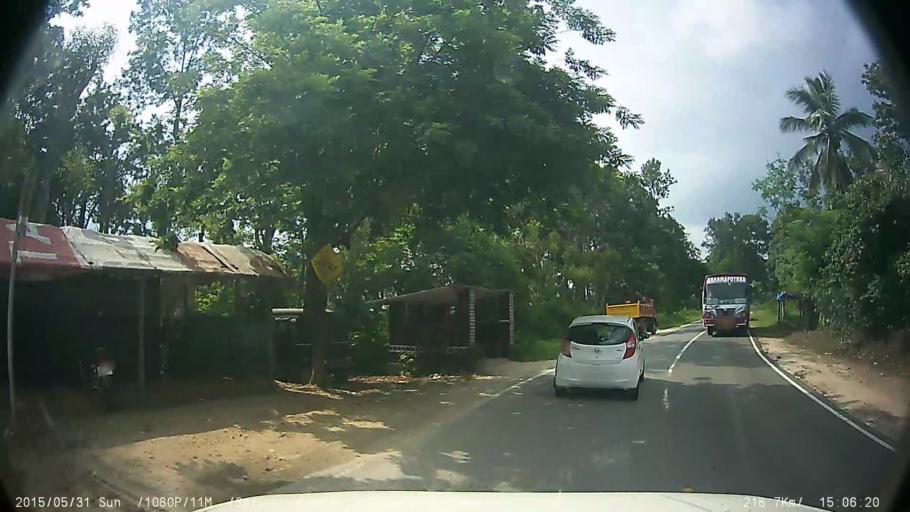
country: IN
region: Kerala
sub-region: Wayanad
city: Kalpetta
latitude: 11.6414
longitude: 76.2136
